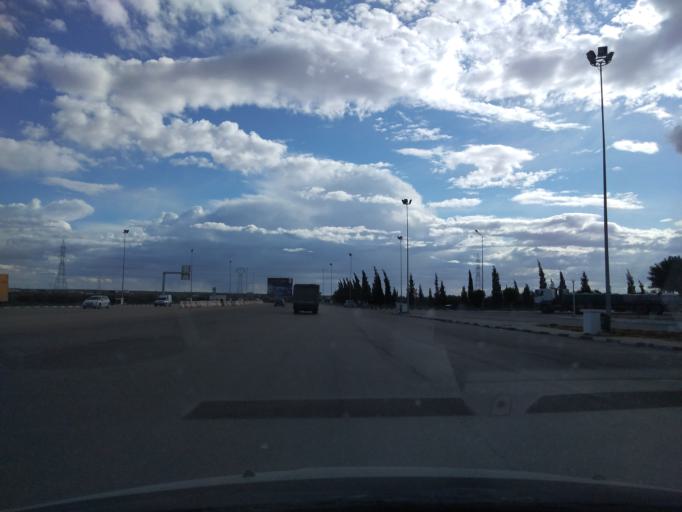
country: TN
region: Susah
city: Masakin
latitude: 35.6892
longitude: 10.5627
